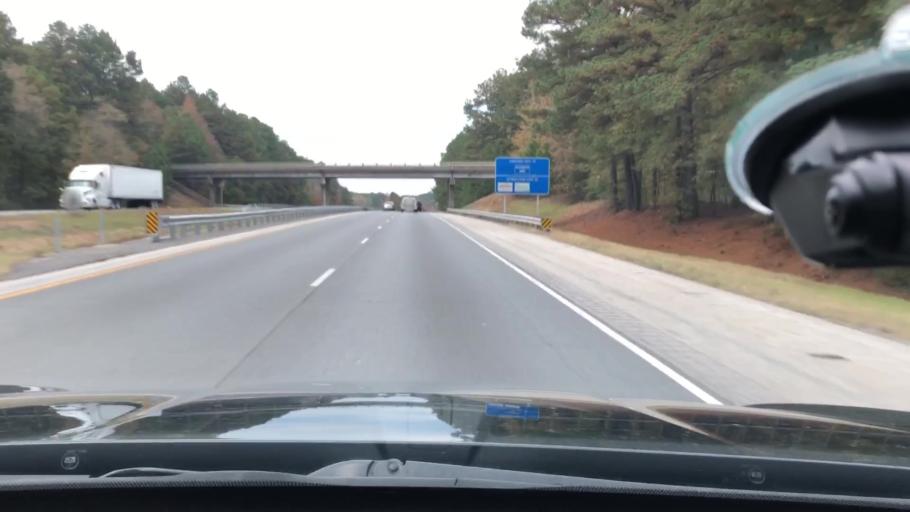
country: US
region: Arkansas
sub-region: Clark County
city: Arkadelphia
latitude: 34.0914
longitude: -93.1087
